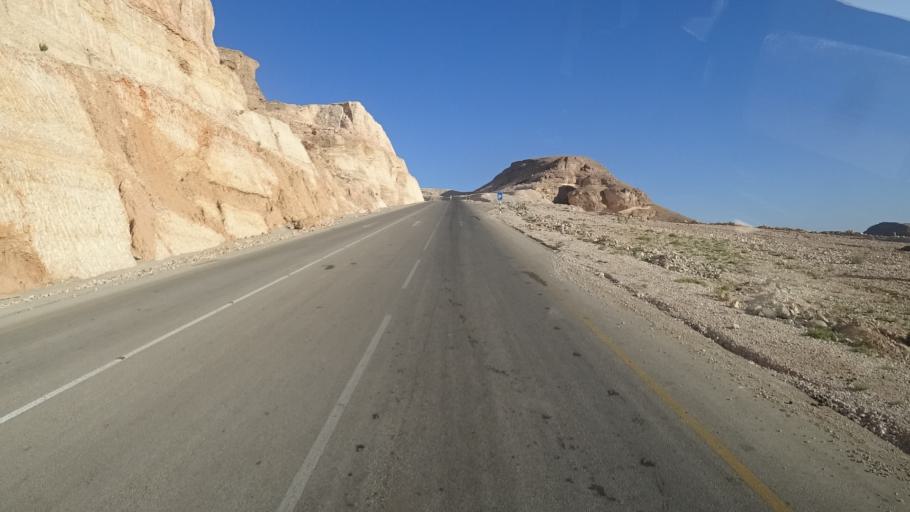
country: YE
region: Al Mahrah
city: Hawf
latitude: 17.0936
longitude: 53.0601
